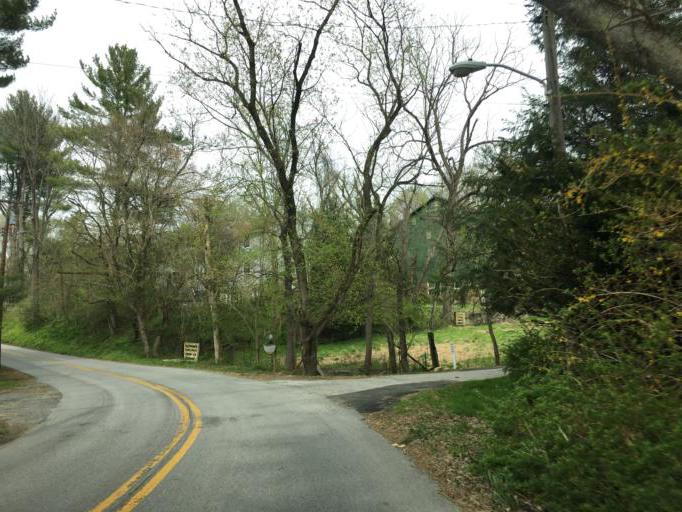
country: US
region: Maryland
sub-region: Baltimore County
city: Hunt Valley
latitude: 39.5509
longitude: -76.6331
